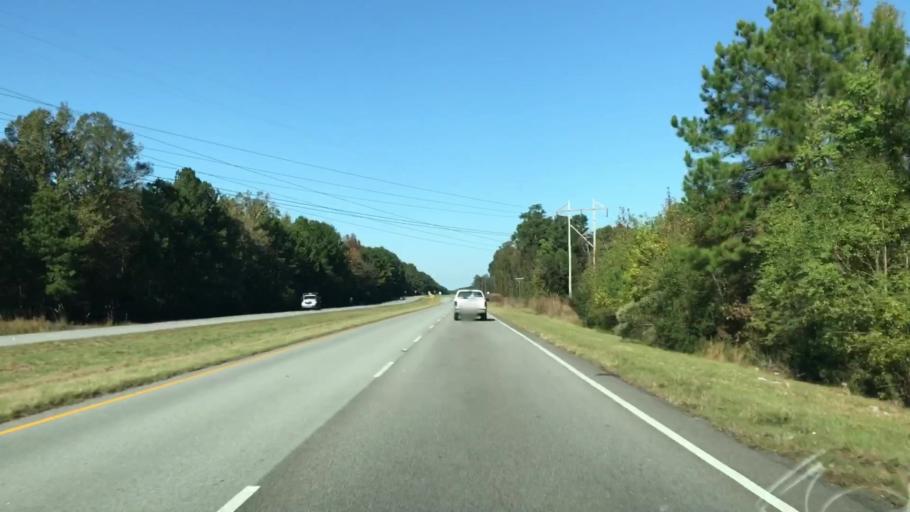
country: US
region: South Carolina
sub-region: Hampton County
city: Yemassee
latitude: 32.6091
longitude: -80.8091
